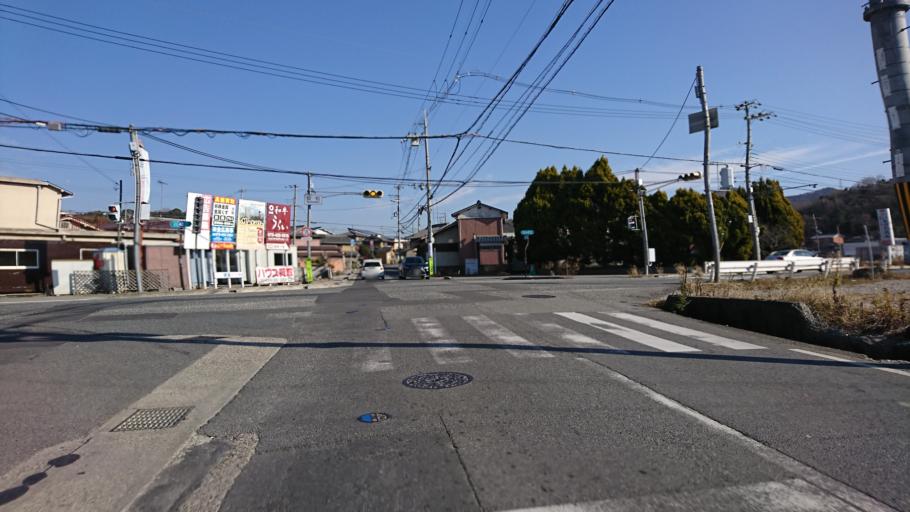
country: JP
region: Hyogo
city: Kakogawacho-honmachi
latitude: 34.8146
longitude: 134.8355
